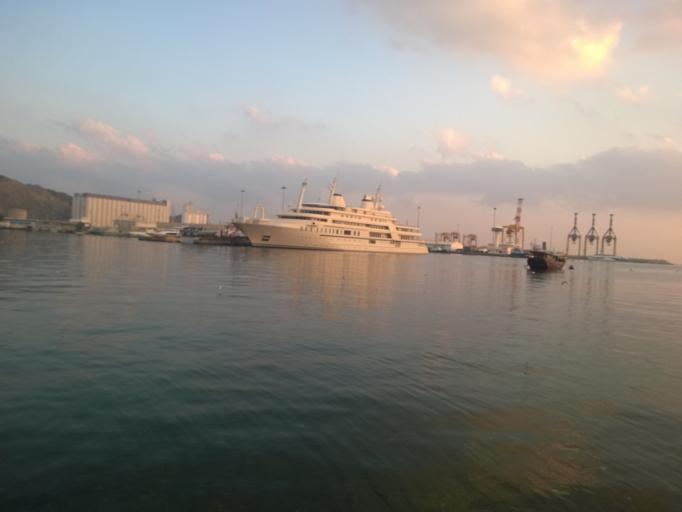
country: OM
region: Muhafazat Masqat
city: Muscat
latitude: 23.6207
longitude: 58.5644
